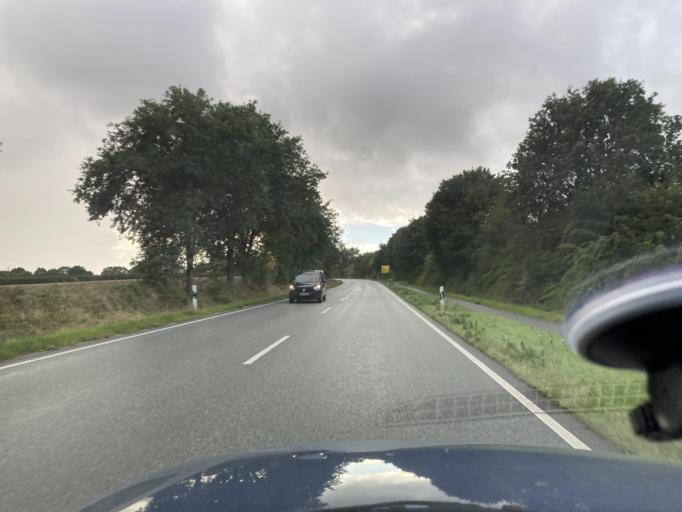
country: DE
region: Schleswig-Holstein
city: Suderdorf
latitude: 54.2193
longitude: 9.3529
